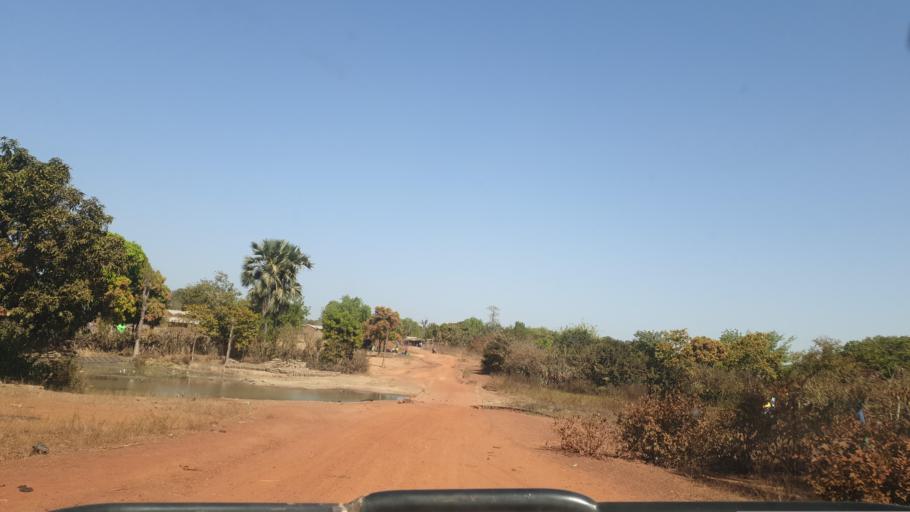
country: ML
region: Koulikoro
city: Dioila
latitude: 11.8937
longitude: -6.9803
